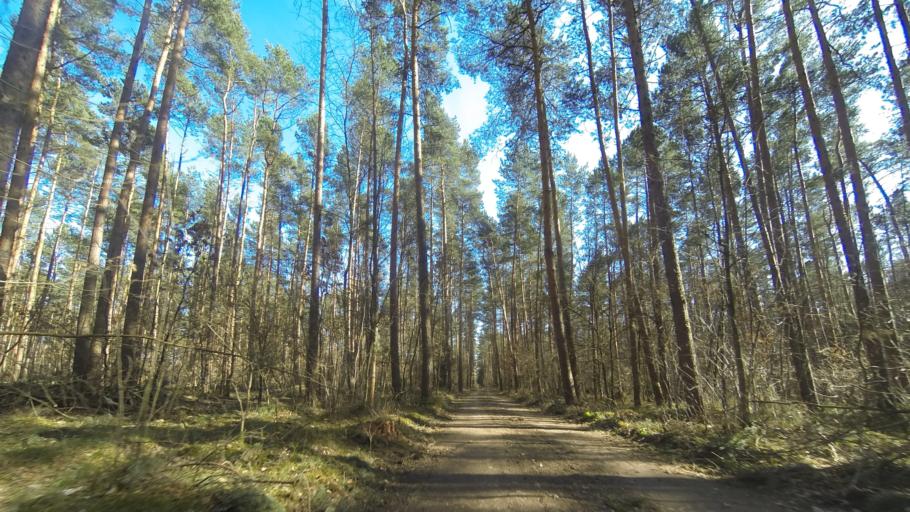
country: DE
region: Saxony
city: Laussnitz
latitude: 51.2631
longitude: 13.8506
